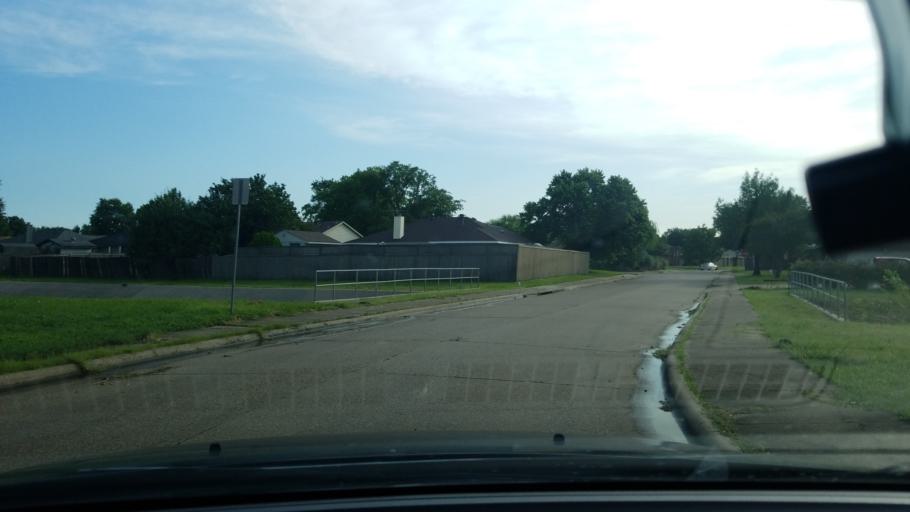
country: US
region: Texas
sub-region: Dallas County
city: Mesquite
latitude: 32.8020
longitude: -96.6088
